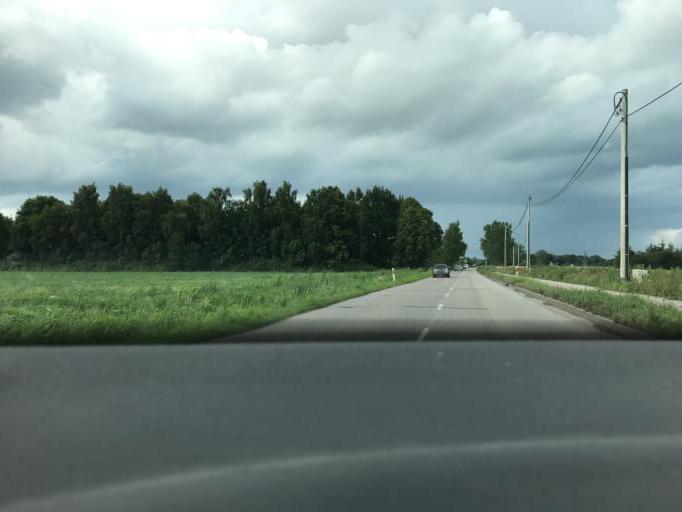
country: PL
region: Pomeranian Voivodeship
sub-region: Gdansk
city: Gdansk
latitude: 54.2984
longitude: 18.7219
